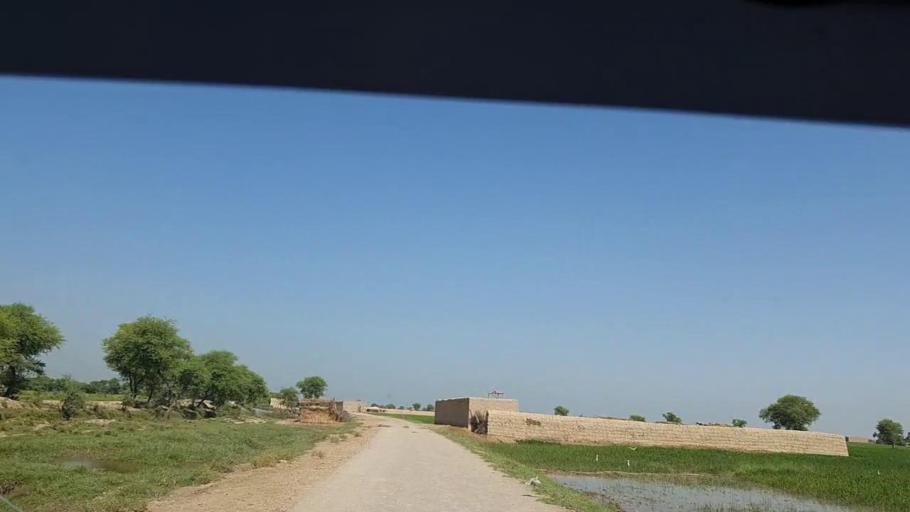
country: PK
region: Sindh
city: Tangwani
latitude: 28.2917
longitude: 69.0871
